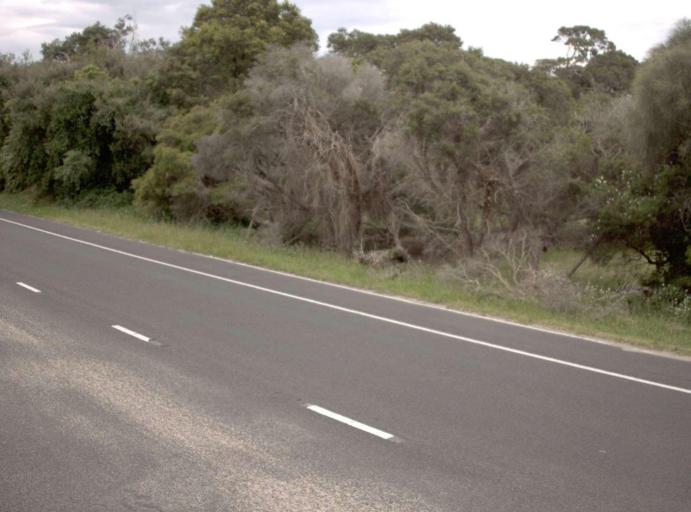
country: AU
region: Victoria
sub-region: Mornington Peninsula
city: Blairgowrie
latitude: -38.3552
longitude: 144.7636
